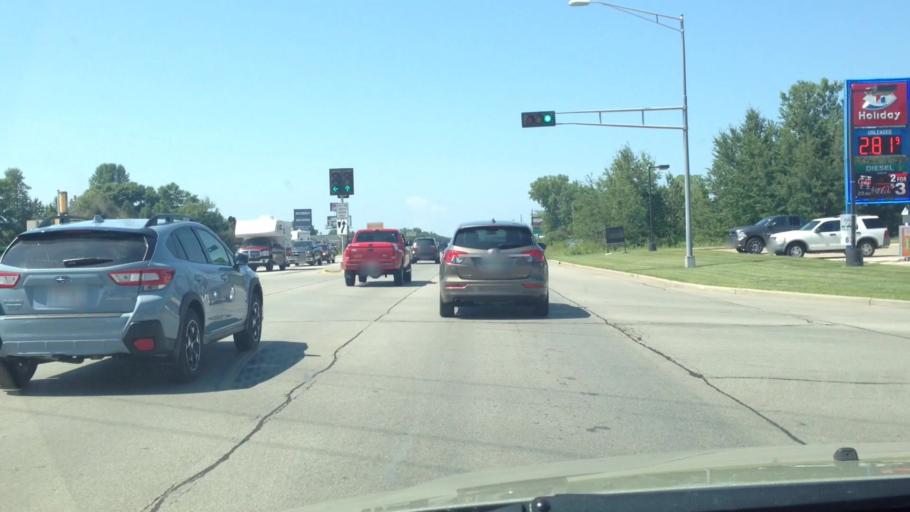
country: US
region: Wisconsin
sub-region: Marinette County
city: Marinette
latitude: 45.0828
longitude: -87.6603
